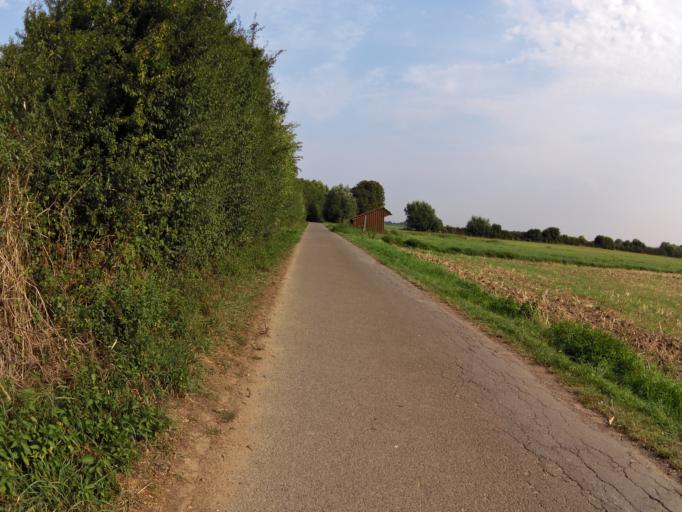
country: DE
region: Lower Saxony
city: Raddestorf
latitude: 52.4592
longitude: 9.0171
